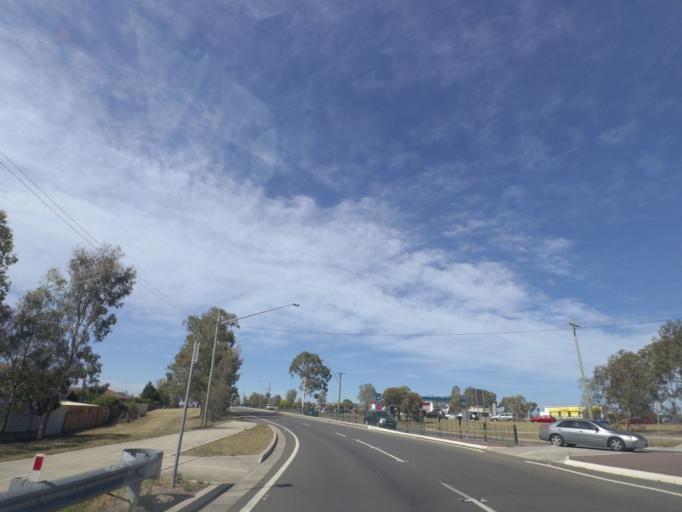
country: AU
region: New South Wales
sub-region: Campbelltown Municipality
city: Leumeah
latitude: -34.0305
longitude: 150.8306
